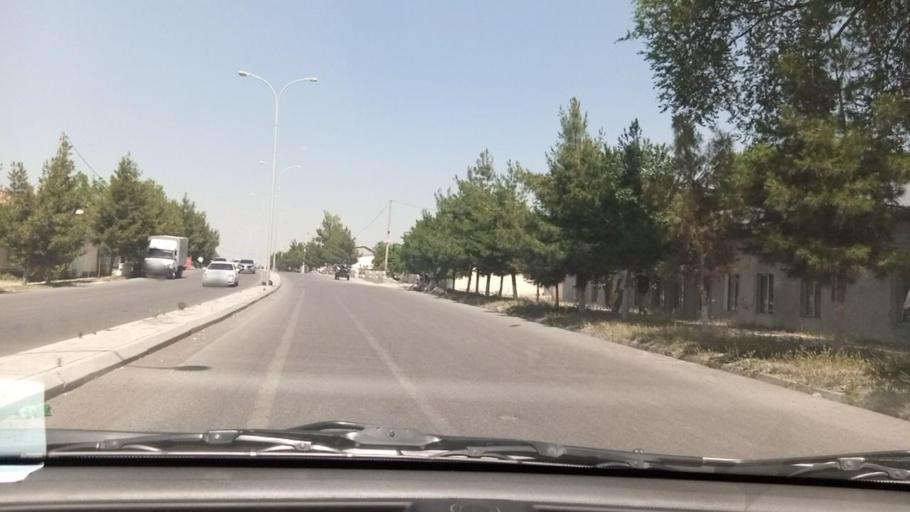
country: UZ
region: Toshkent Shahri
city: Tashkent
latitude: 41.2398
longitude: 69.1954
